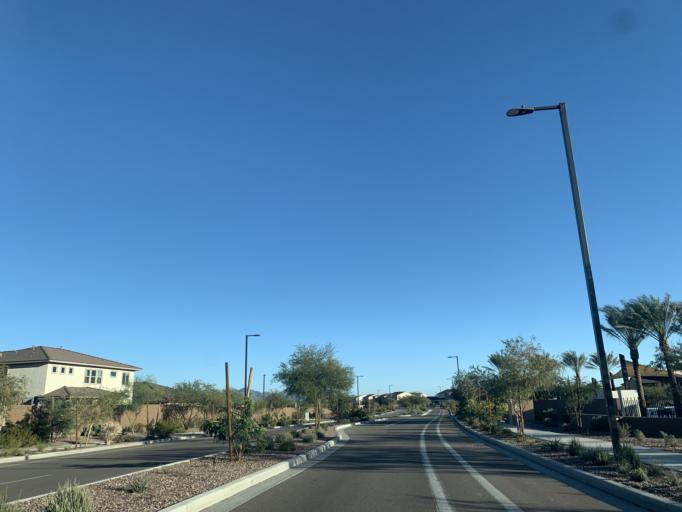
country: US
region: Arizona
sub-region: Maricopa County
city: Cave Creek
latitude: 33.6886
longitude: -112.0140
